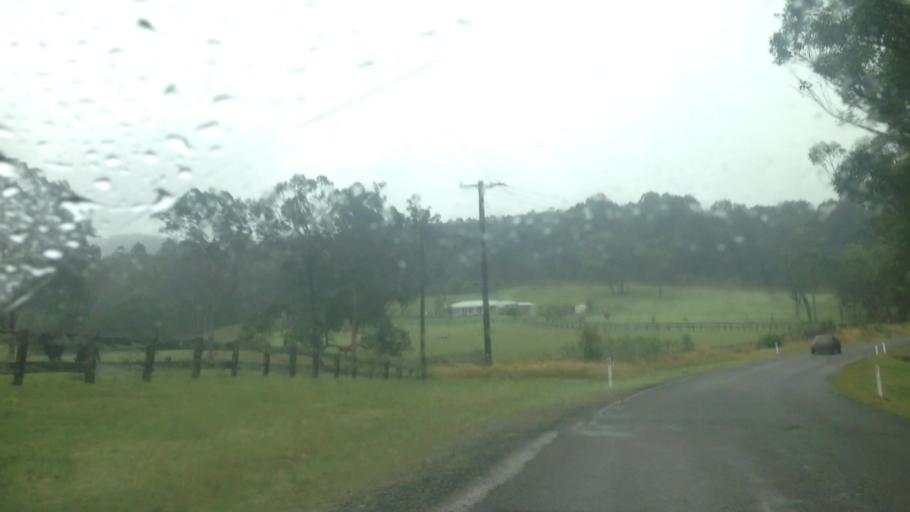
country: AU
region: New South Wales
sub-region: Wyong Shire
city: Little Jilliby
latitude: -33.1963
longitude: 151.3587
